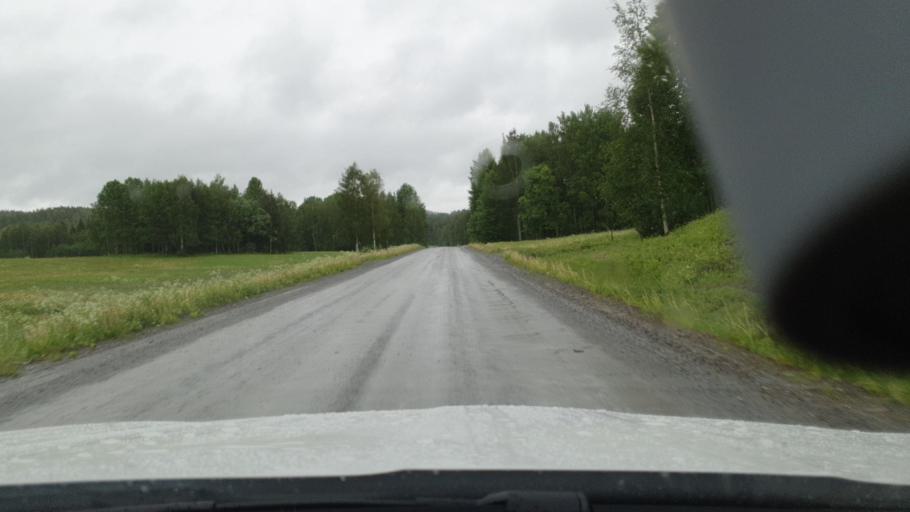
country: SE
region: Vaesterbotten
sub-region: Skelleftea Kommun
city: Burtraesk
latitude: 64.3661
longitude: 20.4030
